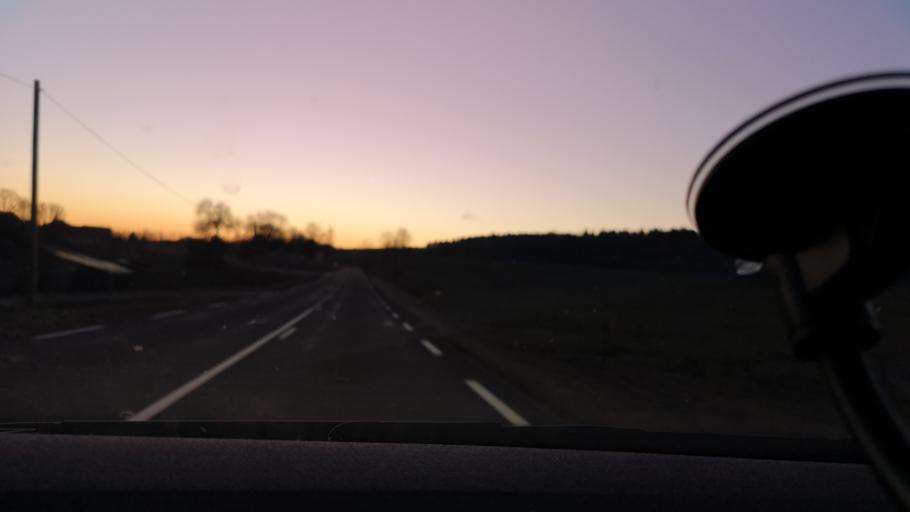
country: FR
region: Franche-Comte
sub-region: Departement du Doubs
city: Frasne
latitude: 46.8119
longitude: 6.0355
